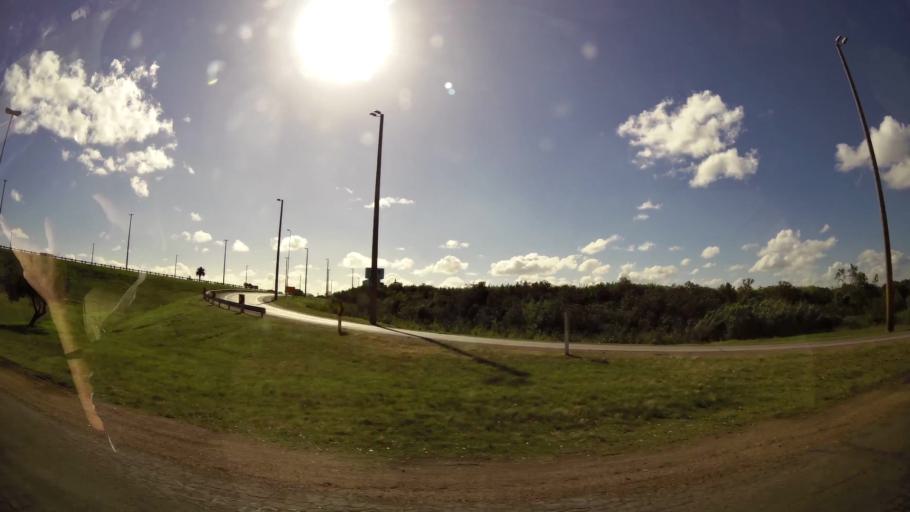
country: UY
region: Montevideo
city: Montevideo
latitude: -34.8561
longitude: -56.2562
